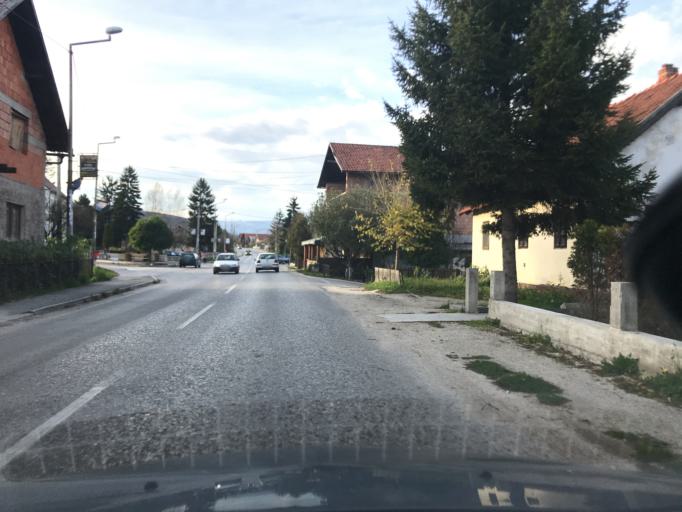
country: BA
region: Federation of Bosnia and Herzegovina
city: Vitez
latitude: 44.1600
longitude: 17.7842
